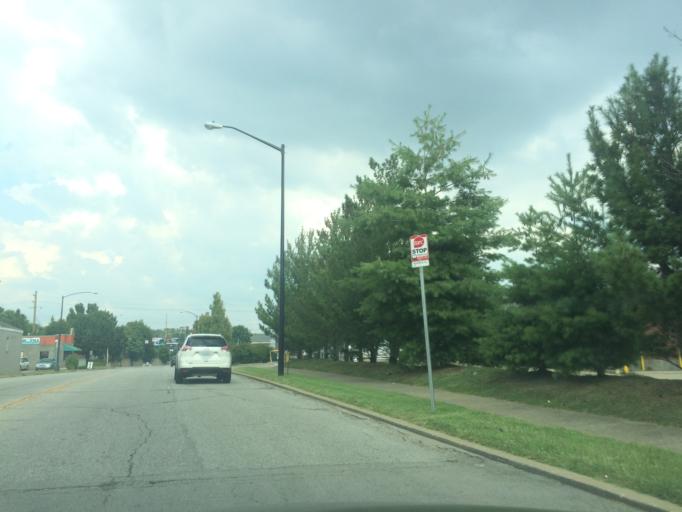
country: US
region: Kentucky
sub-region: Jefferson County
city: Louisville
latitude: 38.2255
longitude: -85.7569
